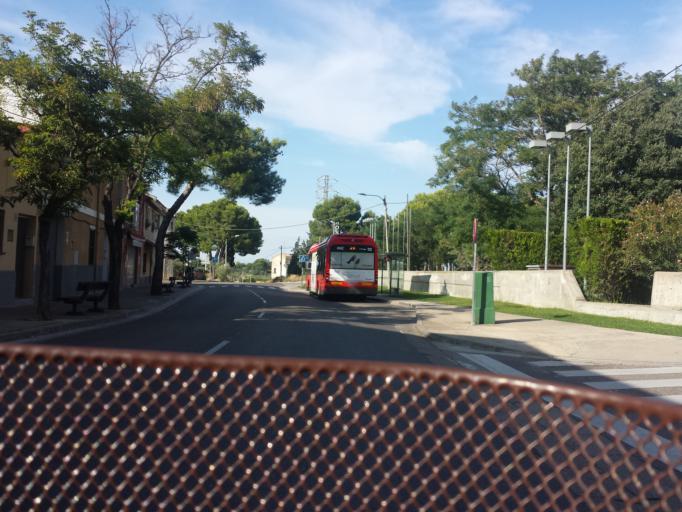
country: ES
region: Aragon
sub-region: Provincia de Zaragoza
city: Zaragoza
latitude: 41.6922
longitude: -0.8625
